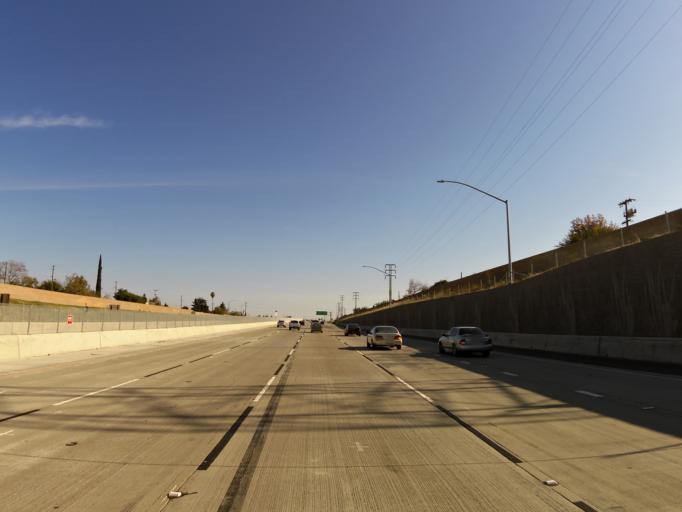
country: US
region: California
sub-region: Contra Costa County
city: Antioch
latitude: 37.9981
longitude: -121.8155
